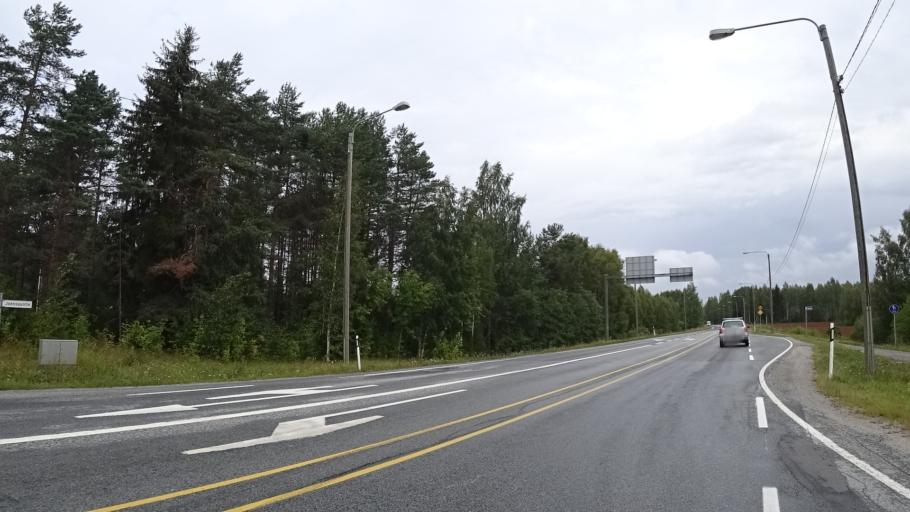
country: FI
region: Southern Savonia
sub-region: Savonlinna
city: Kerimaeki
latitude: 61.9264
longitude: 29.2713
